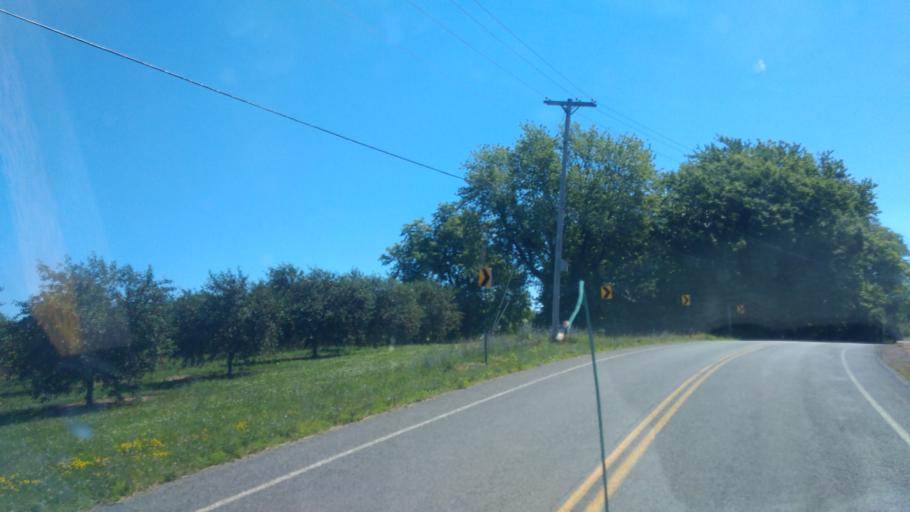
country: US
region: New York
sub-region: Wayne County
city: Sodus
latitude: 43.2712
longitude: -77.0812
